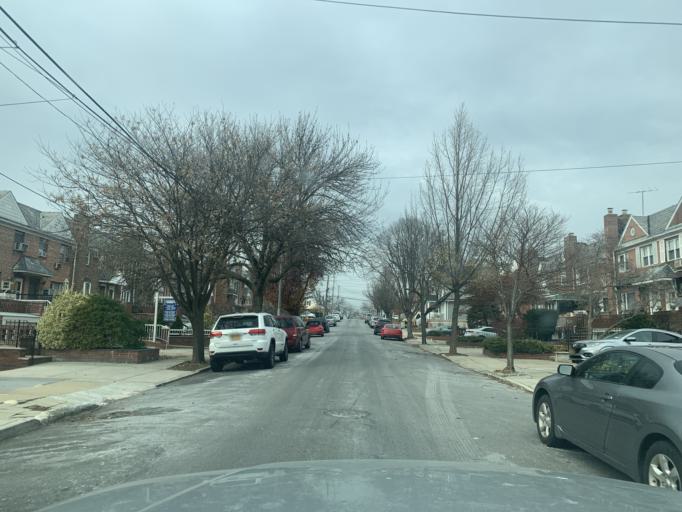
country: US
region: New York
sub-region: Kings County
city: East New York
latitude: 40.7258
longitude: -73.8810
